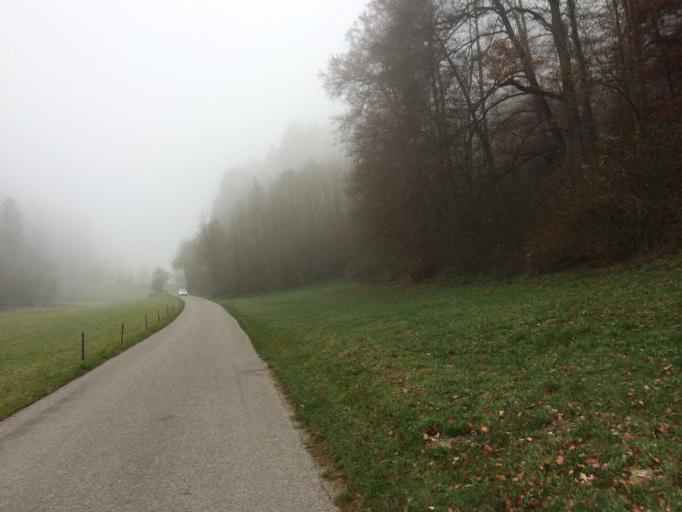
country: CH
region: Bern
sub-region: Bern-Mittelland District
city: Koniz
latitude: 46.9137
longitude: 7.4309
